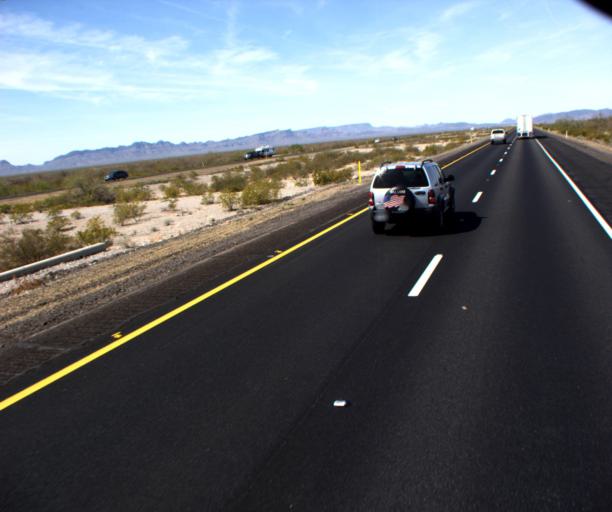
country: US
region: Arizona
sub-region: La Paz County
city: Salome
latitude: 33.6231
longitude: -113.7123
